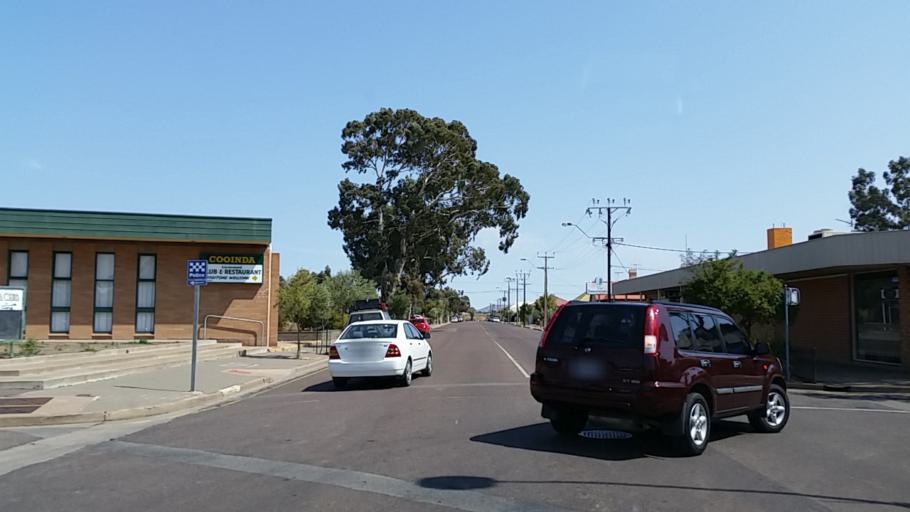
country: AU
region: South Australia
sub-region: Port Augusta
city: Port Augusta
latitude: -32.4937
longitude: 137.7639
